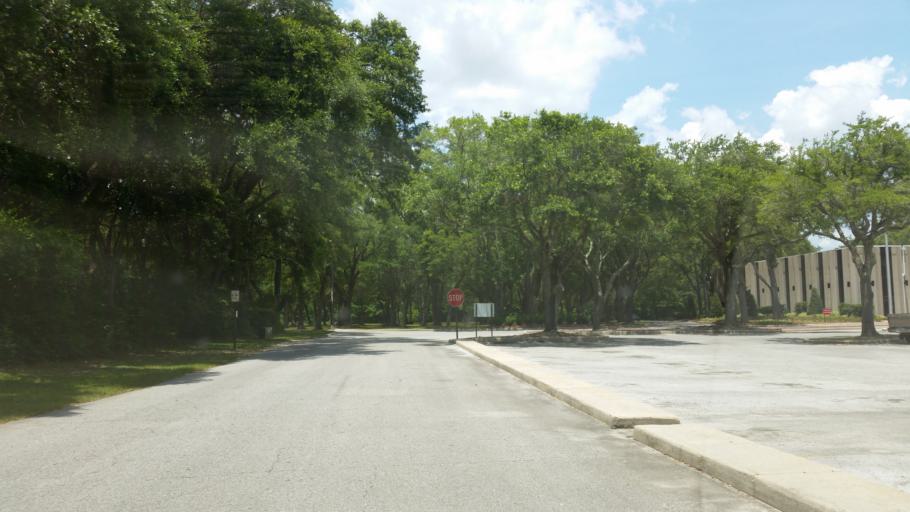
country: US
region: Florida
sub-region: Escambia County
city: Ferry Pass
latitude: 30.5008
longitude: -87.2187
